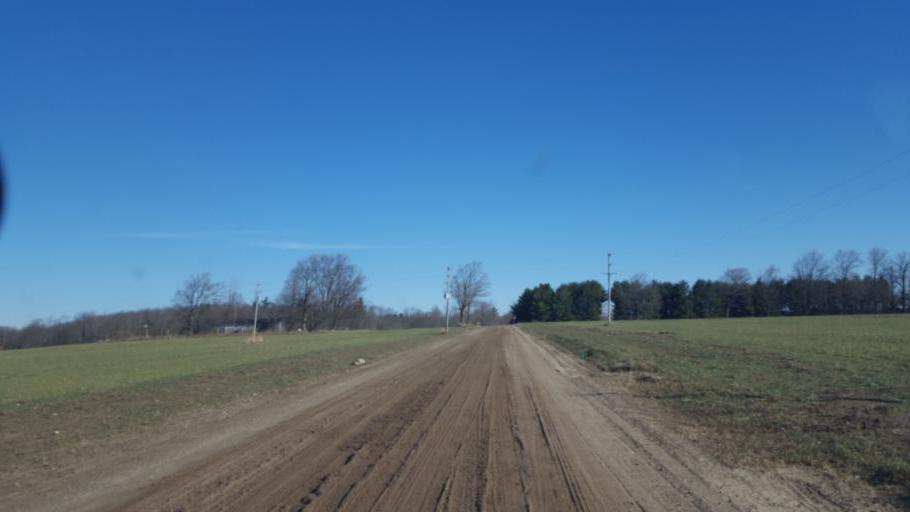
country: US
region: Michigan
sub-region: Montcalm County
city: Edmore
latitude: 43.5074
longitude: -85.0654
